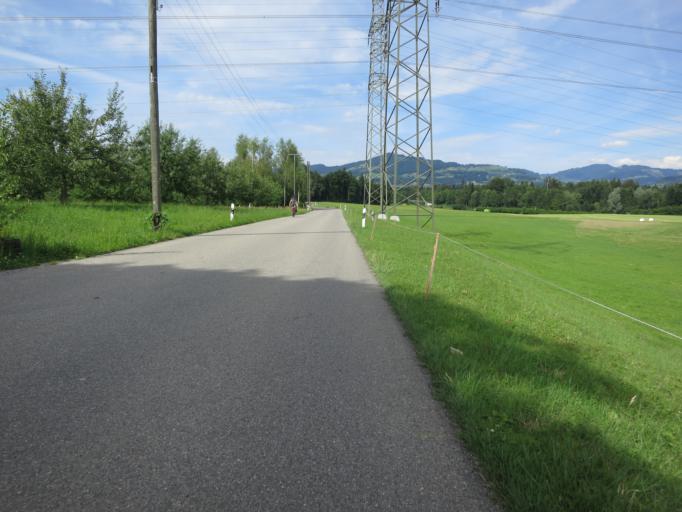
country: CH
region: Zurich
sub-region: Bezirk Hinwil
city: Bubikon
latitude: 47.2531
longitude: 8.8217
